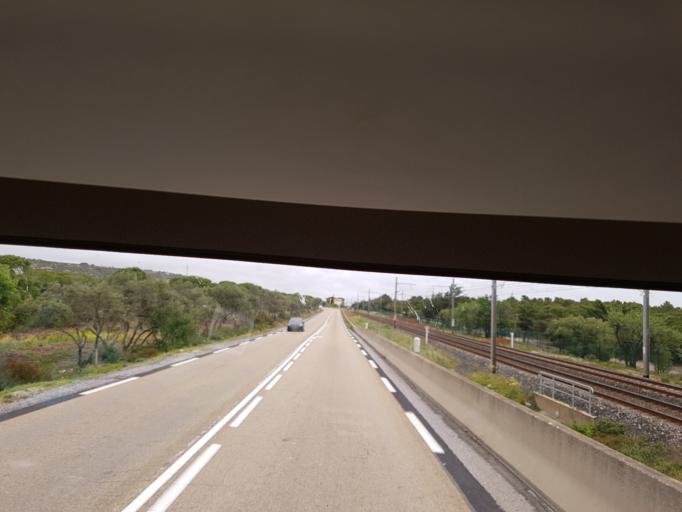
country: FR
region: Languedoc-Roussillon
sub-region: Departement de l'Aude
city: Leucate
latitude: 42.8748
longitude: 2.9925
